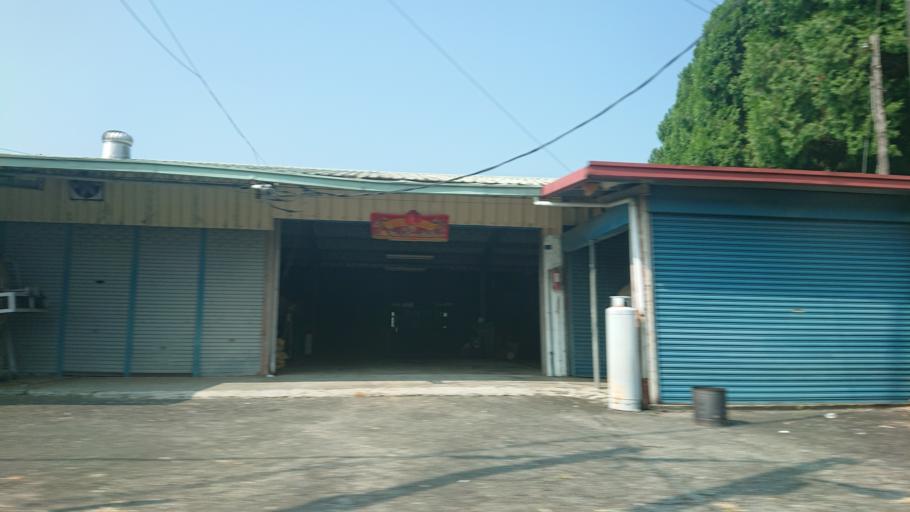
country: TW
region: Taiwan
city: Lugu
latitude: 23.7008
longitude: 120.6629
